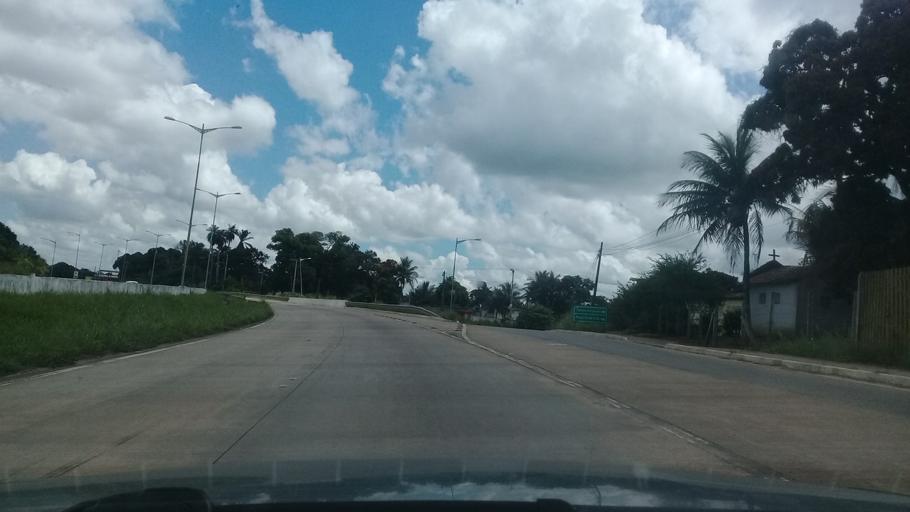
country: BR
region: Pernambuco
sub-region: Sao Lourenco Da Mata
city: Sao Lourenco da Mata
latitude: -7.9345
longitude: -35.1300
